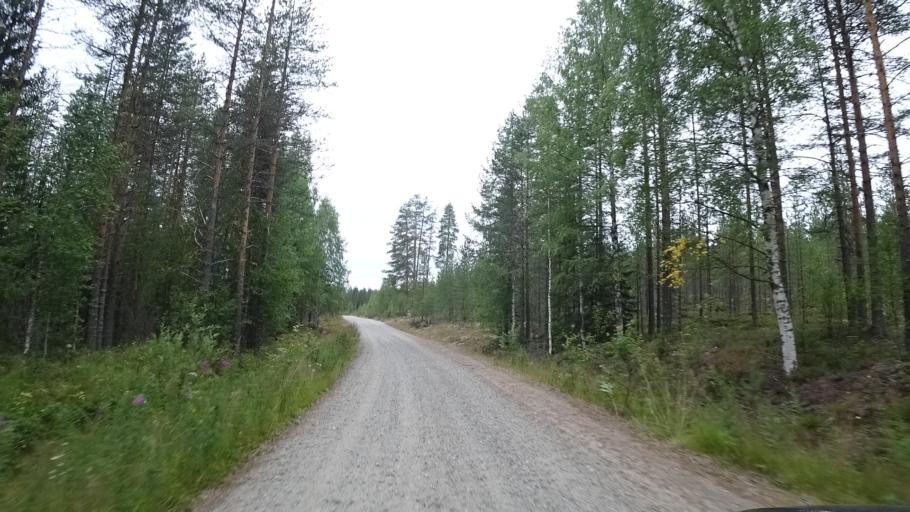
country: FI
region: North Karelia
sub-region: Joensuu
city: Ilomantsi
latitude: 63.1543
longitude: 30.6394
